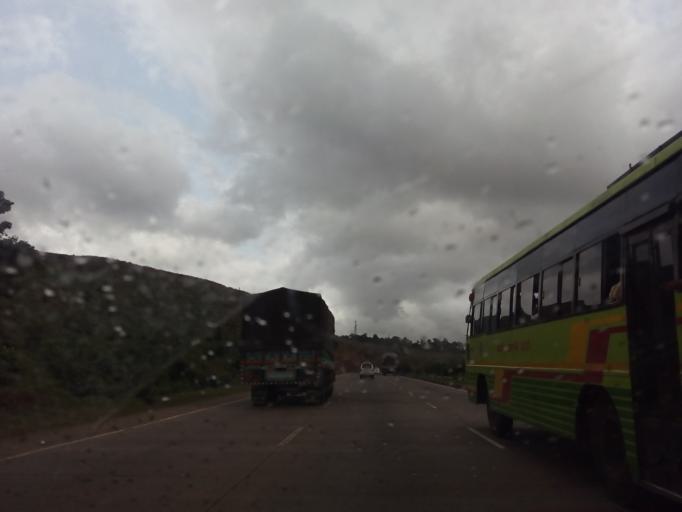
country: IN
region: Karnataka
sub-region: Belgaum
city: Belgaum
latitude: 16.0416
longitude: 74.5292
